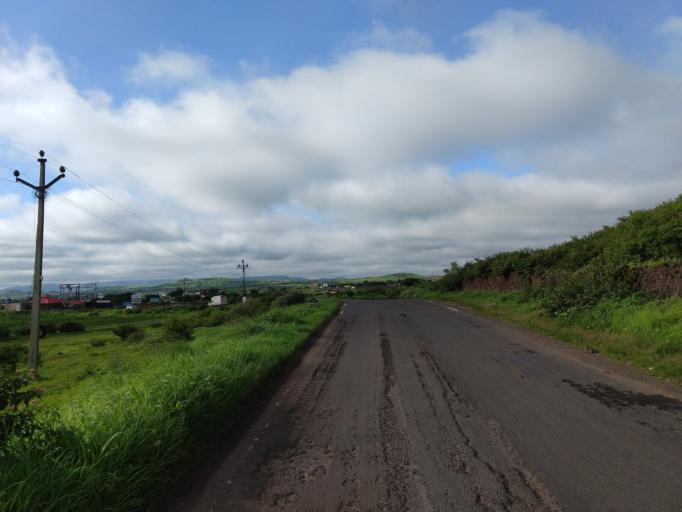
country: IN
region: Maharashtra
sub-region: Pune Division
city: Khed
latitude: 18.4001
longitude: 73.9125
